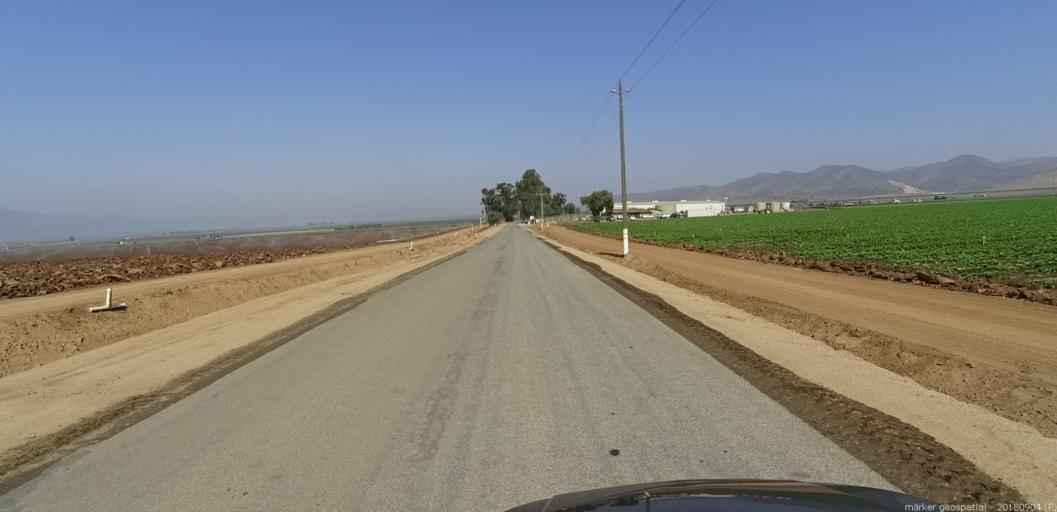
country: US
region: California
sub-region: Monterey County
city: Gonzales
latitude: 36.5351
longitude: -121.4255
